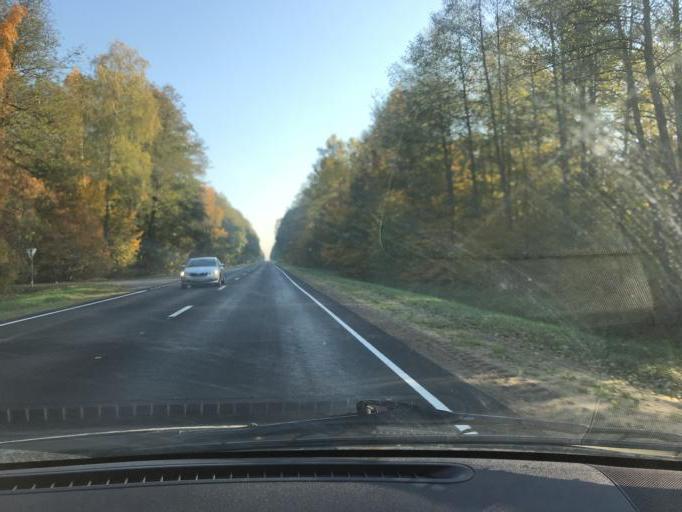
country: BY
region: Brest
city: Baranovichi
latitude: 52.8841
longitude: 25.7877
